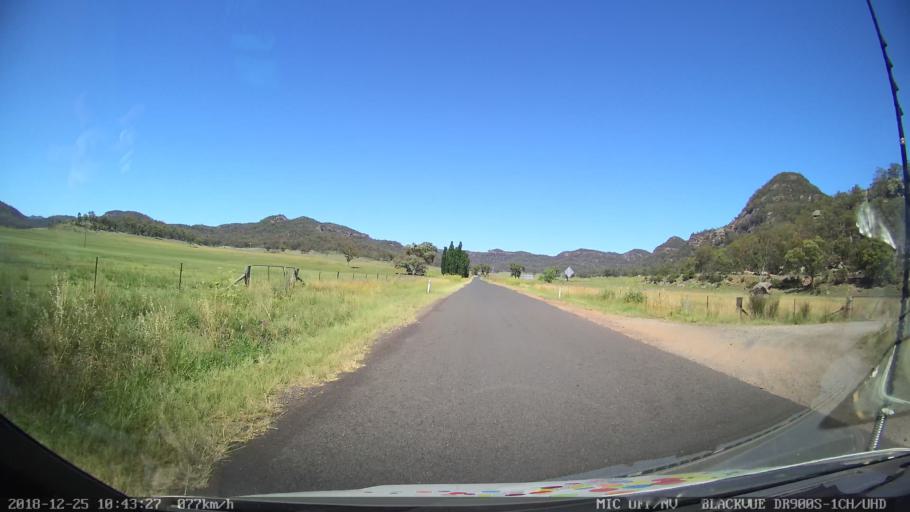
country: AU
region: New South Wales
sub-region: Upper Hunter Shire
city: Merriwa
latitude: -32.4223
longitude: 150.3127
